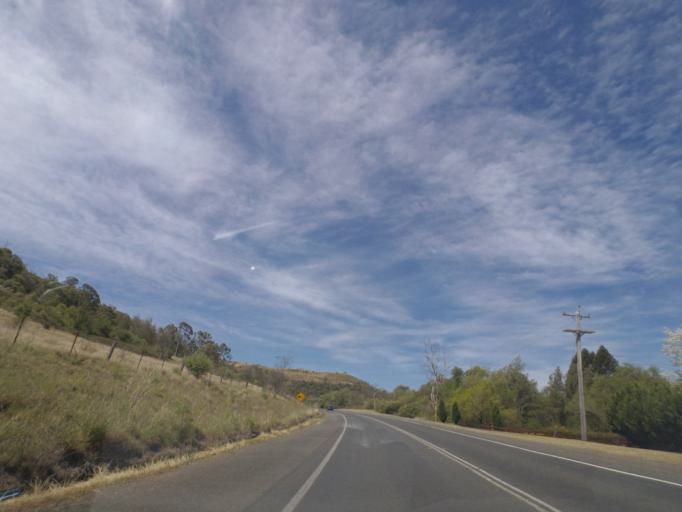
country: AU
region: New South Wales
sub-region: Wollondilly
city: Picton
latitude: -34.1627
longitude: 150.6388
